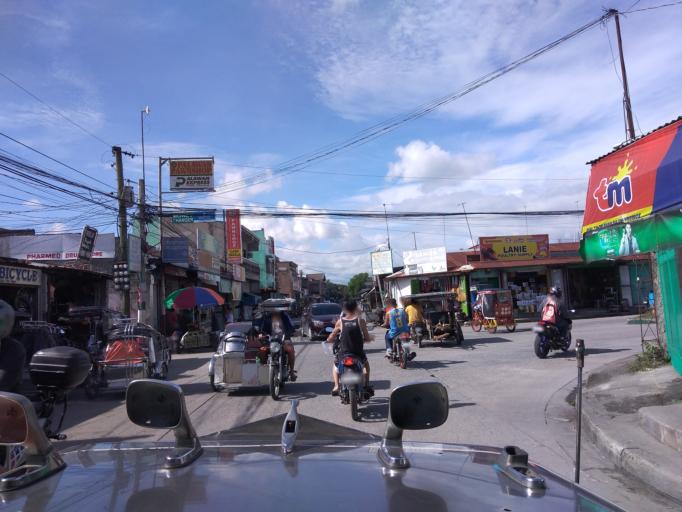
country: PH
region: Central Luzon
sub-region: Province of Pampanga
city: Pandacaqui
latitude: 15.1758
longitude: 120.6480
